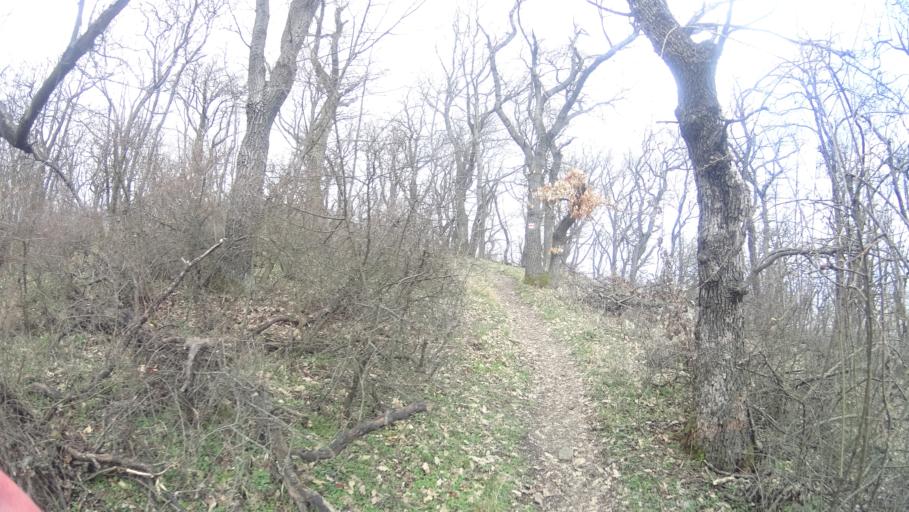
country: HU
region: Pest
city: Leanyfalu
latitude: 47.7302
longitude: 19.0580
